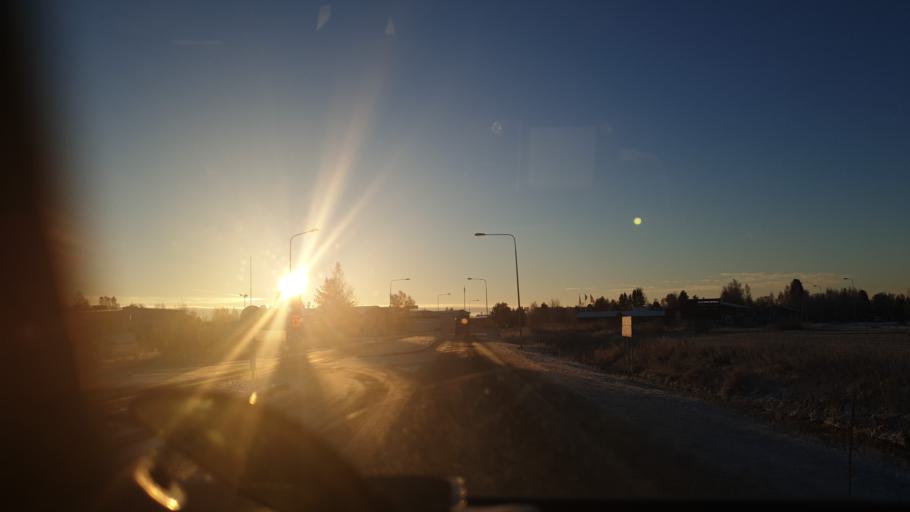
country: FI
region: Northern Ostrobothnia
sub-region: Ylivieska
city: Kalajoki
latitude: 64.2652
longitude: 23.9491
